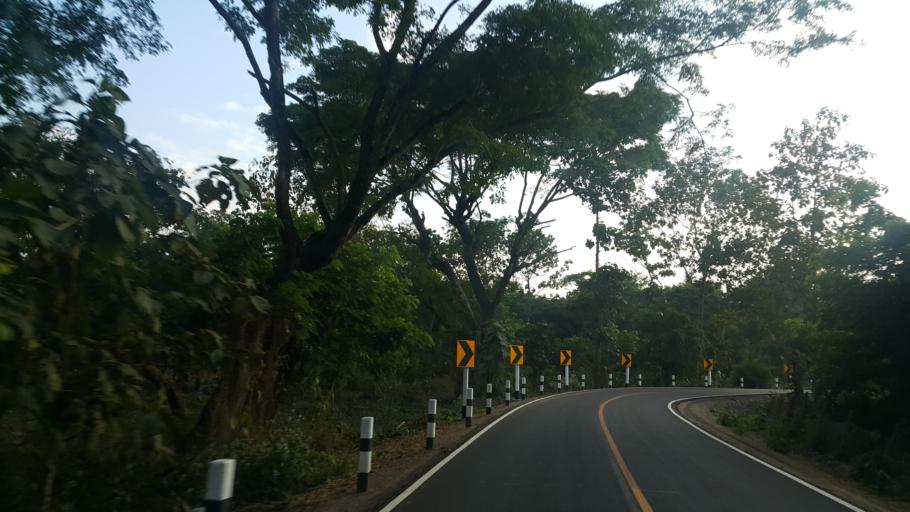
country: TH
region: Lampang
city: Sop Prap
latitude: 17.9303
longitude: 99.3384
